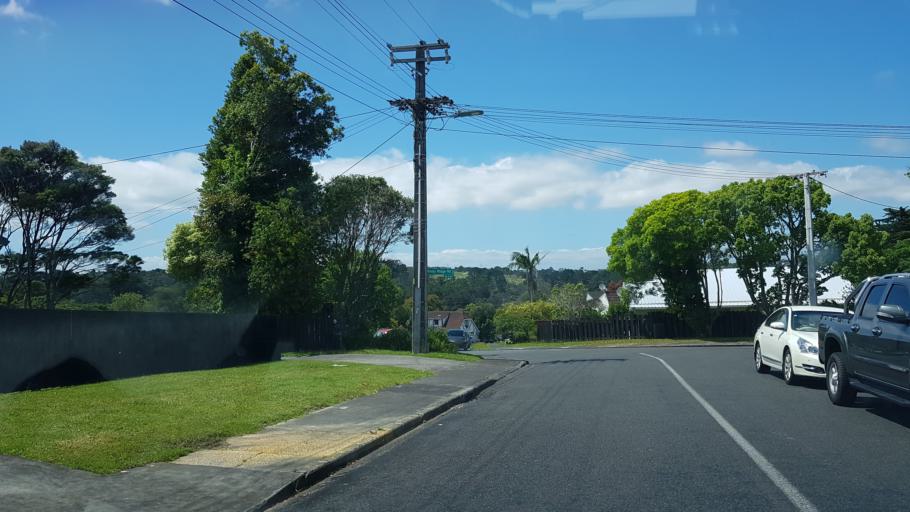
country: NZ
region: Auckland
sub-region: Auckland
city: North Shore
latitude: -36.7912
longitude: 174.7136
